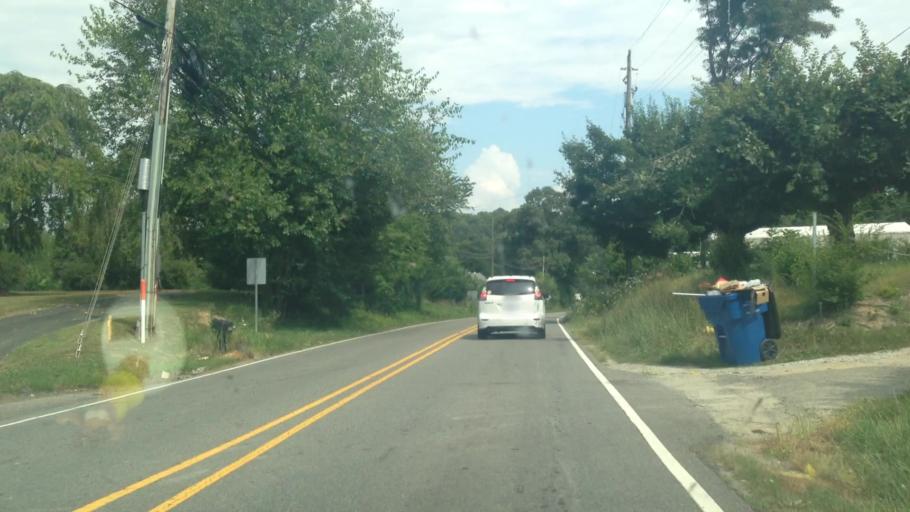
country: US
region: North Carolina
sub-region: Surry County
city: Mount Airy
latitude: 36.4852
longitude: -80.5883
